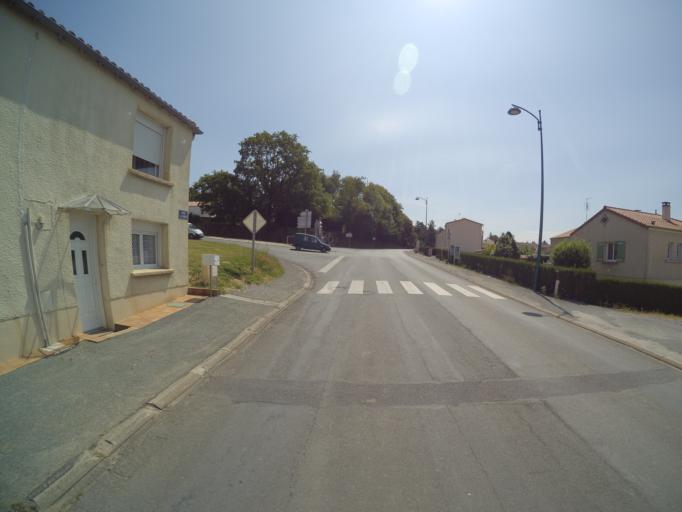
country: FR
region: Pays de la Loire
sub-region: Departement de la Vendee
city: Saint-Michel-Mont-Mercure
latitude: 46.8328
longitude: -0.8868
